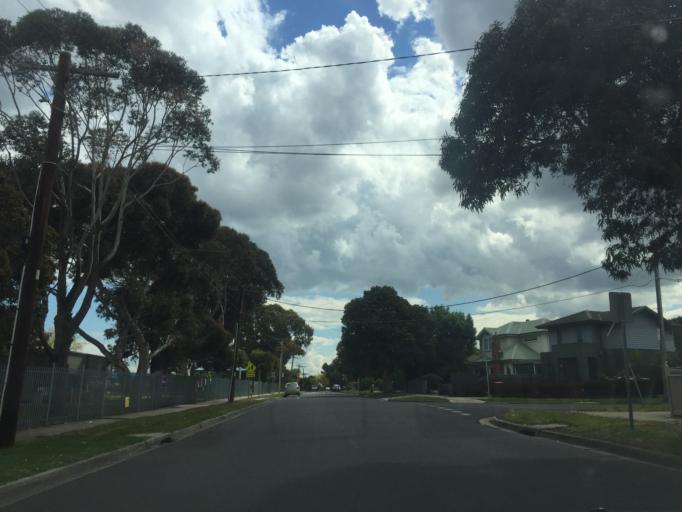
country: AU
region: Victoria
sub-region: Darebin
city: Kingsbury
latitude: -37.7053
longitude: 145.0228
